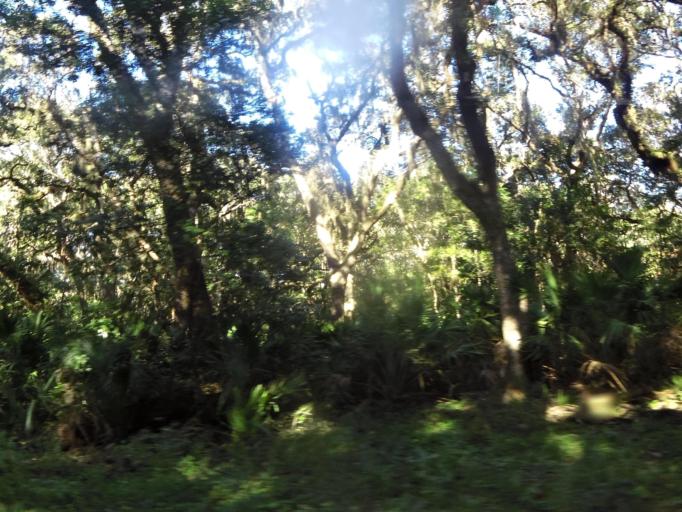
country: US
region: Florida
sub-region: Duval County
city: Atlantic Beach
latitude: 30.4362
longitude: -81.4343
